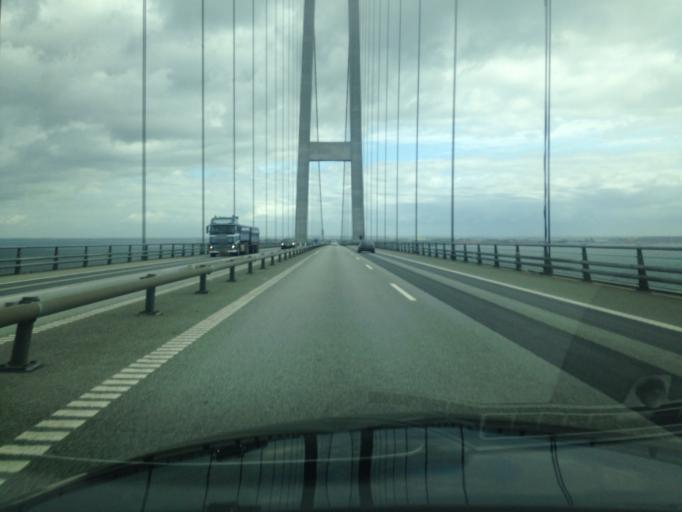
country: DK
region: Zealand
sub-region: Slagelse Kommune
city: Korsor
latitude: 55.3426
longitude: 11.0413
